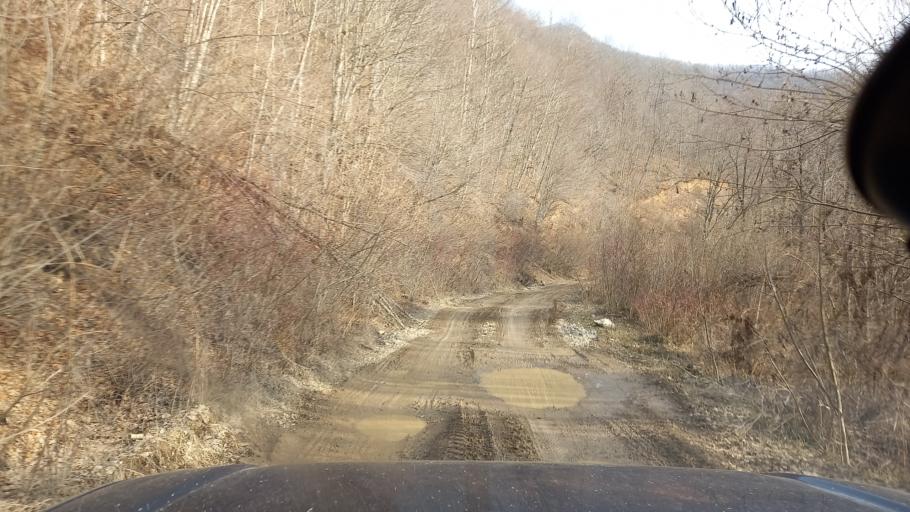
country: RU
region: Adygeya
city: Kamennomostskiy
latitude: 44.1499
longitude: 40.3003
